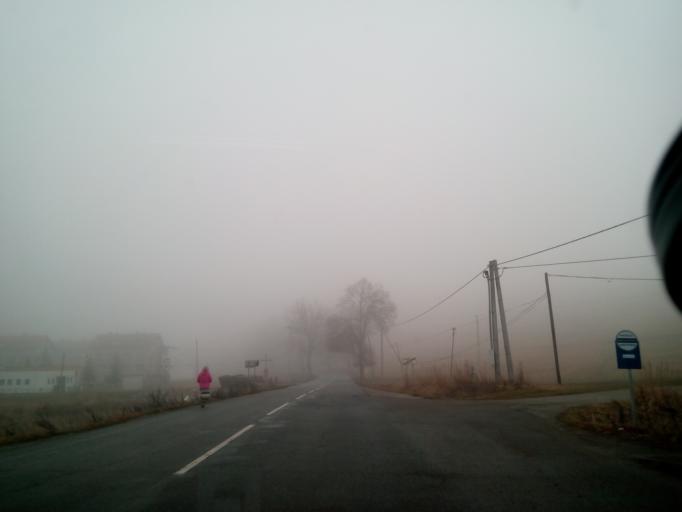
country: SK
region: Presovsky
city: Spisske Podhradie
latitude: 48.9711
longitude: 20.7829
